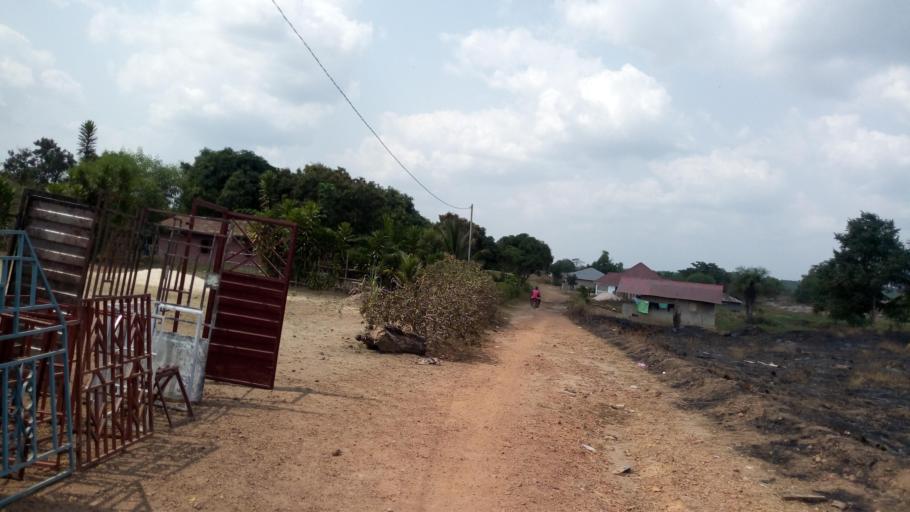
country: SL
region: Southern Province
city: Mogbwemo
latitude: 7.7929
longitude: -12.3021
